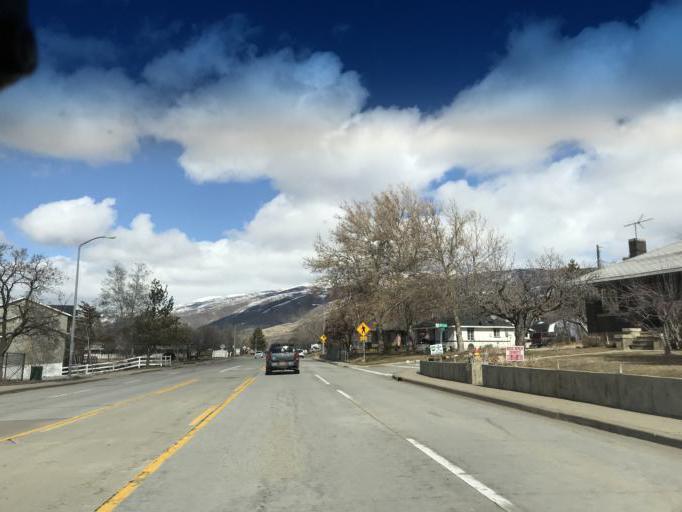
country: US
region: Utah
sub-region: Davis County
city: Bountiful
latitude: 40.8737
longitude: -111.8755
